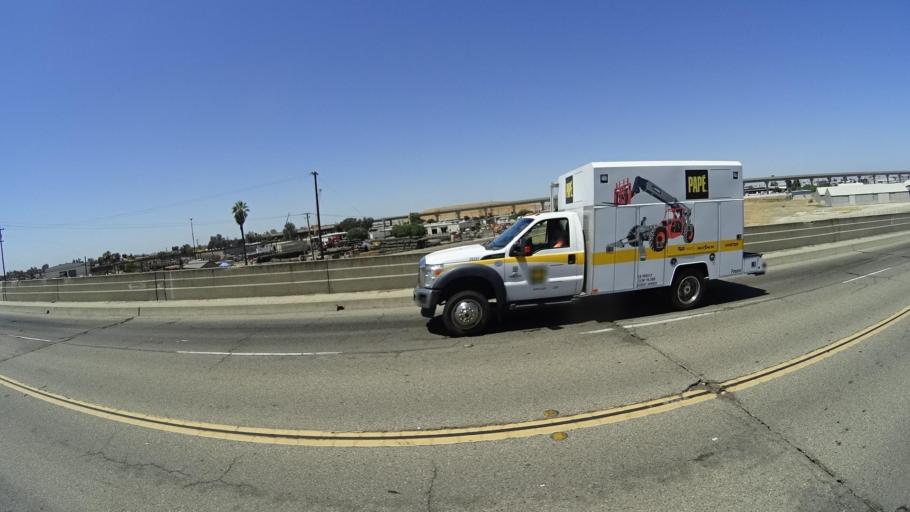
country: US
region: California
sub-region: Fresno County
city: Fresno
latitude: 36.6932
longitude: -119.7509
